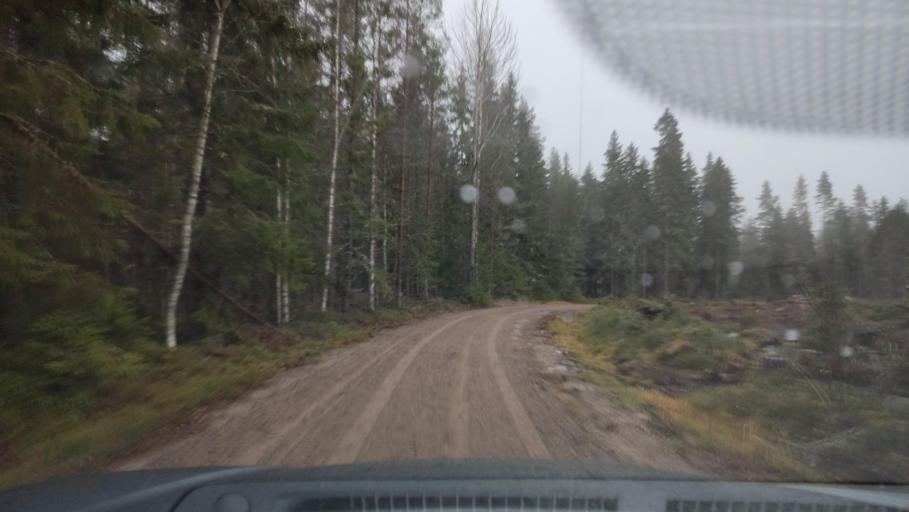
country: FI
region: Southern Ostrobothnia
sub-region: Suupohja
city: Karijoki
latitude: 62.1982
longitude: 21.7799
